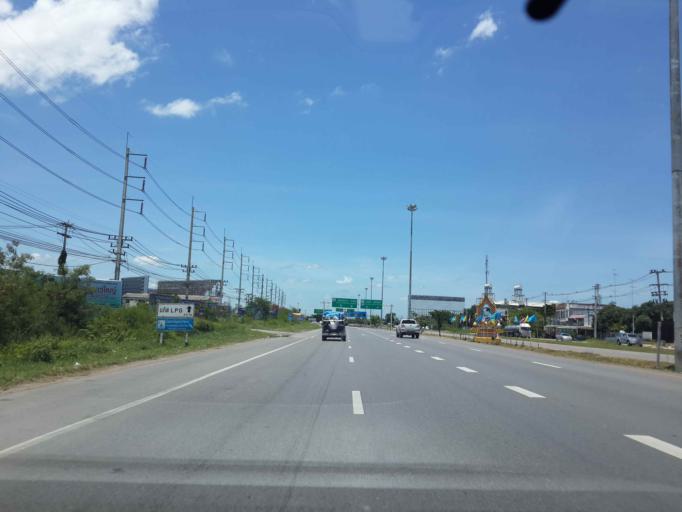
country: TH
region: Ratchaburi
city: Pak Tho
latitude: 13.3323
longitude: 99.8297
